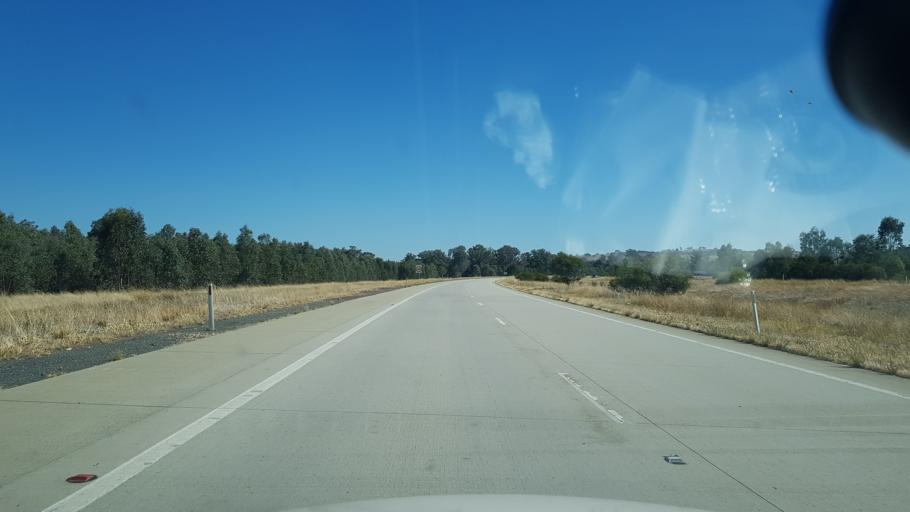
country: AU
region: New South Wales
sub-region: Greater Hume Shire
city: Holbrook
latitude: -35.9123
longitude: 147.1535
